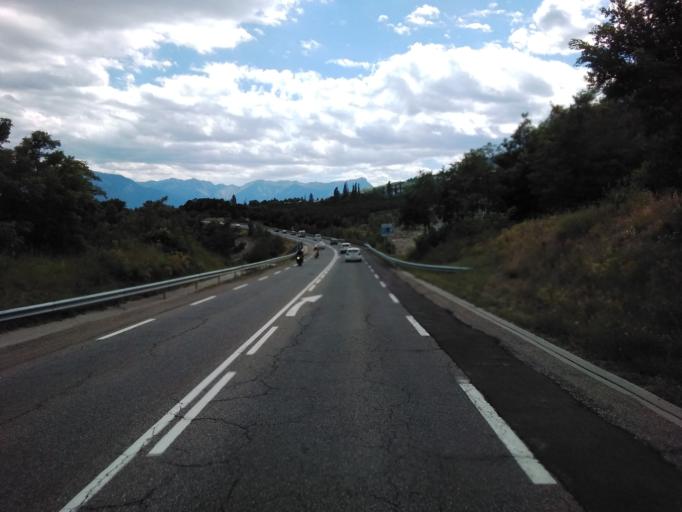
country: FR
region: Provence-Alpes-Cote d'Azur
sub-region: Departement des Hautes-Alpes
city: Embrun
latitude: 44.6210
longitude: 6.5349
